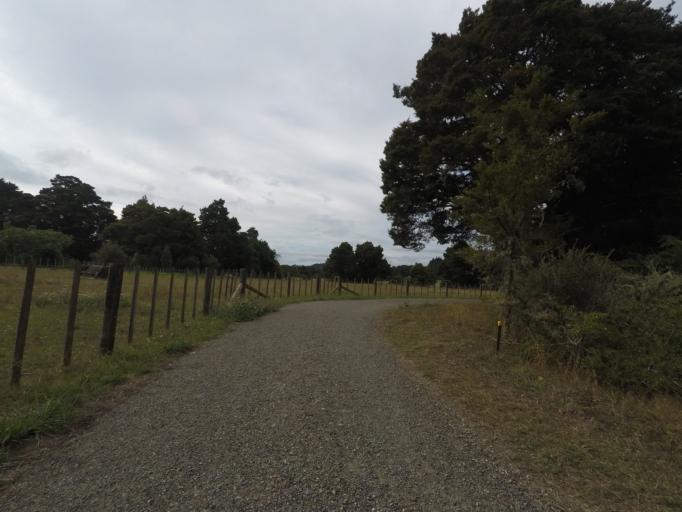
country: NZ
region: Northland
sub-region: Whangarei
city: Whangarei
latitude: -35.6780
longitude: 174.3342
